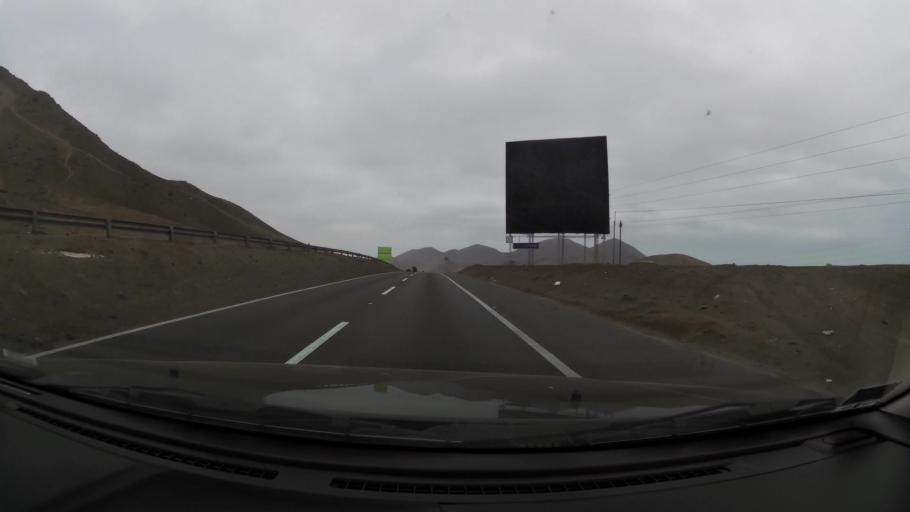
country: PE
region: Lima
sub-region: Lima
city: San Bartolo
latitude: -12.4355
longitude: -76.7550
